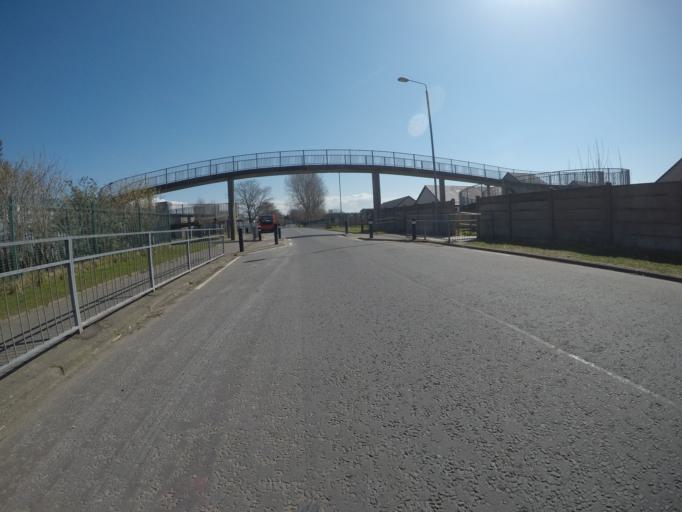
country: GB
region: Scotland
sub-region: North Ayrshire
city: Irvine
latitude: 55.6294
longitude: -4.6660
